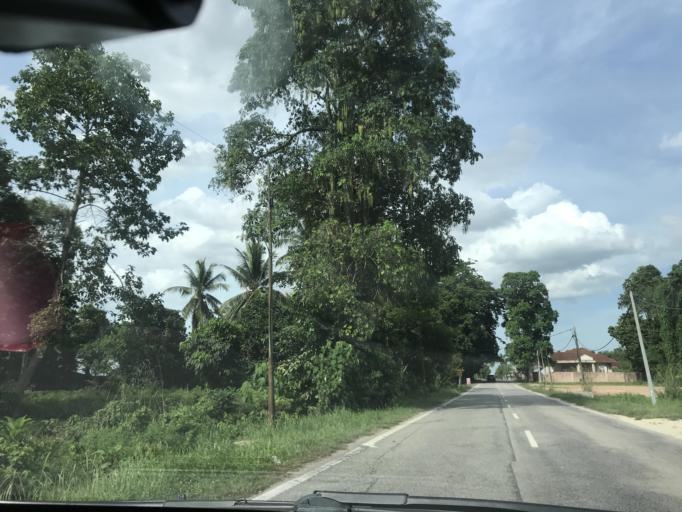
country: MY
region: Kelantan
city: Kampung Lemal
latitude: 6.0332
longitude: 102.1664
